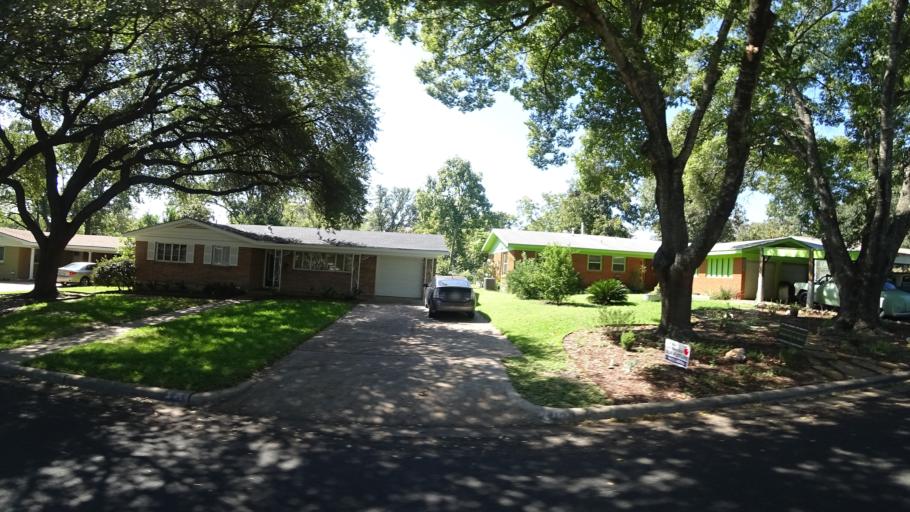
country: US
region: Texas
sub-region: Travis County
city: Austin
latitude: 30.3130
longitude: -97.6976
